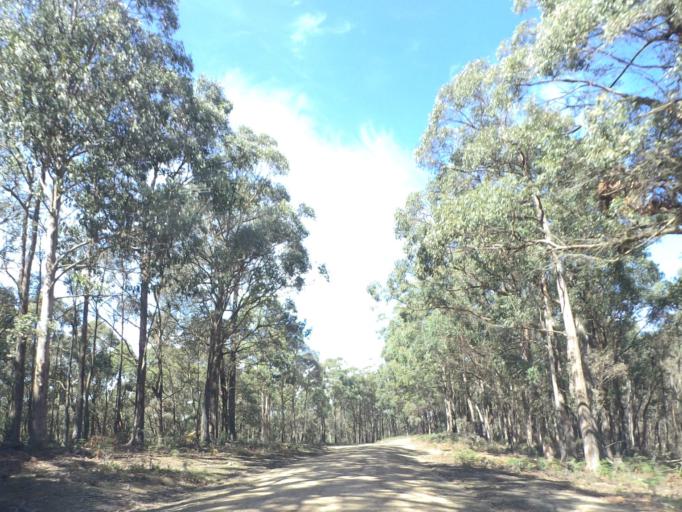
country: AU
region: Victoria
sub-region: Moorabool
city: Bacchus Marsh
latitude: -37.4403
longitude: 144.3777
